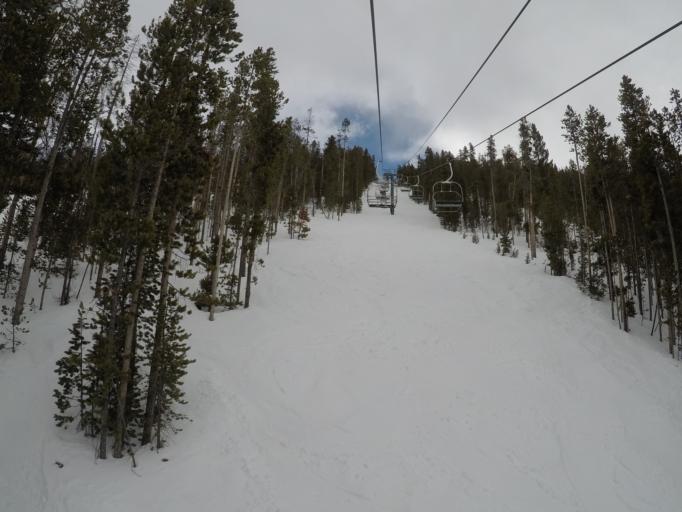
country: US
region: Montana
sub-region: Granite County
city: Philipsburg
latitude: 46.2571
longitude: -113.2444
